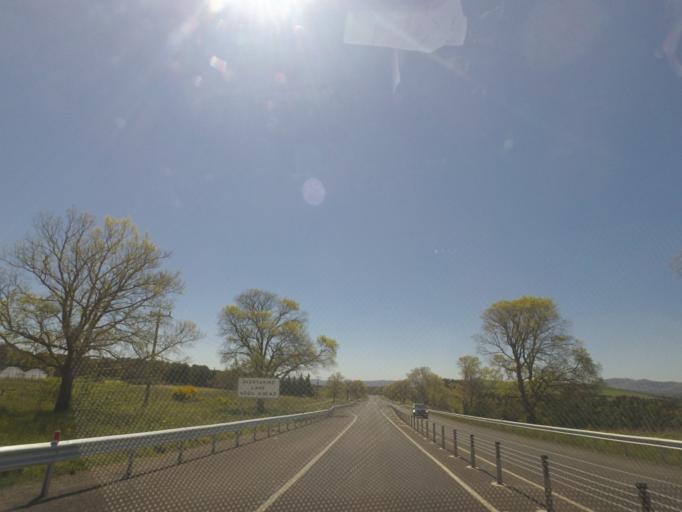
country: AU
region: Victoria
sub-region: Hume
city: Sunbury
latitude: -37.3156
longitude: 144.7404
